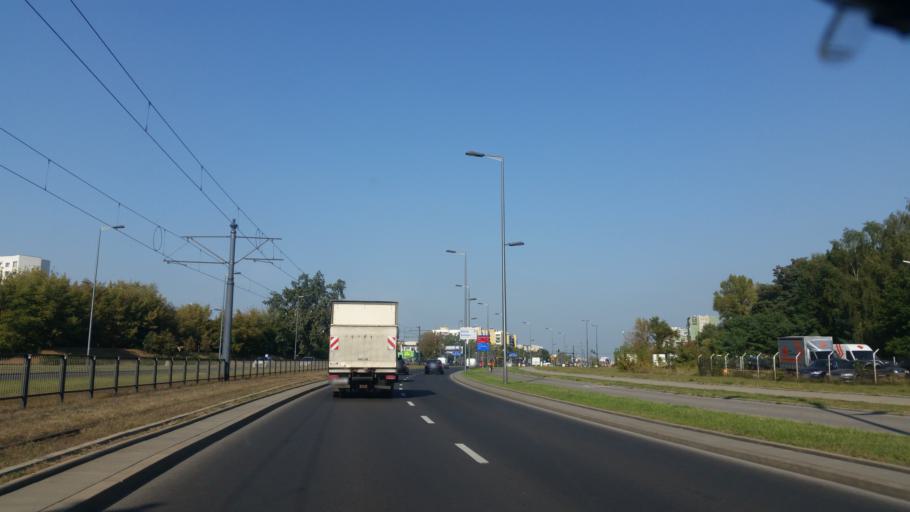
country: PL
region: Masovian Voivodeship
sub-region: Warszawa
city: Bemowo
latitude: 52.2501
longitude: 20.9112
